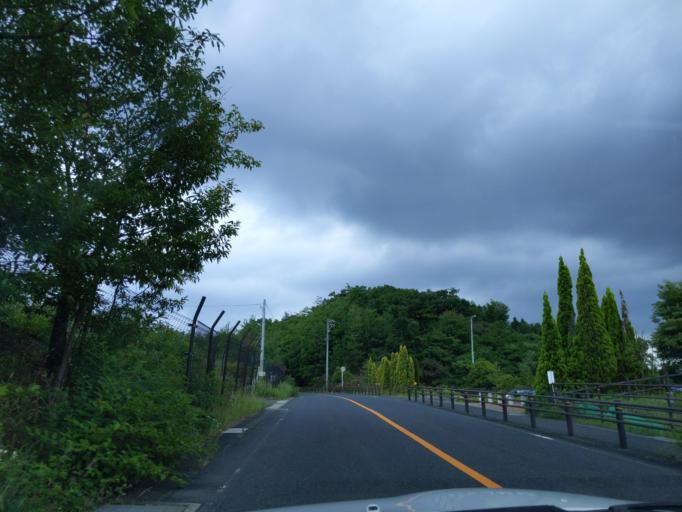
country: JP
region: Aichi
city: Seto
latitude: 35.1869
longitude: 137.1090
